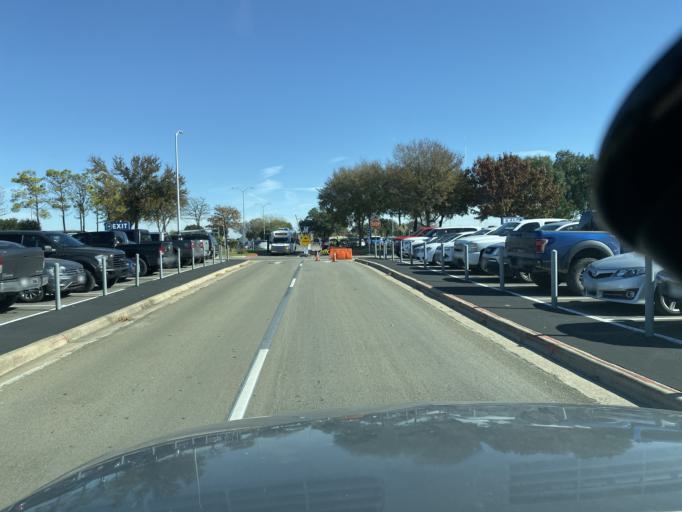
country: US
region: Texas
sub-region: Travis County
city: Hornsby Bend
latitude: 30.2081
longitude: -97.6678
